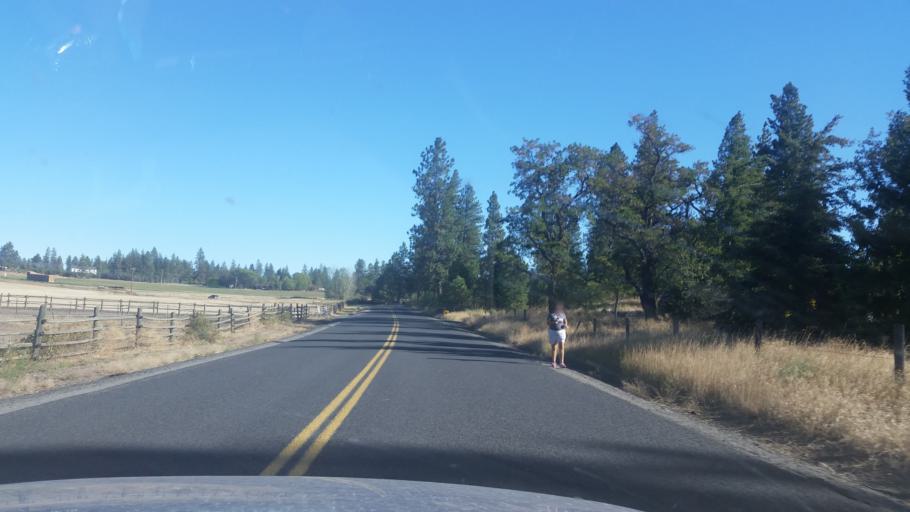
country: US
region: Washington
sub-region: Spokane County
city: Cheney
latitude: 47.5379
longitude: -117.4748
